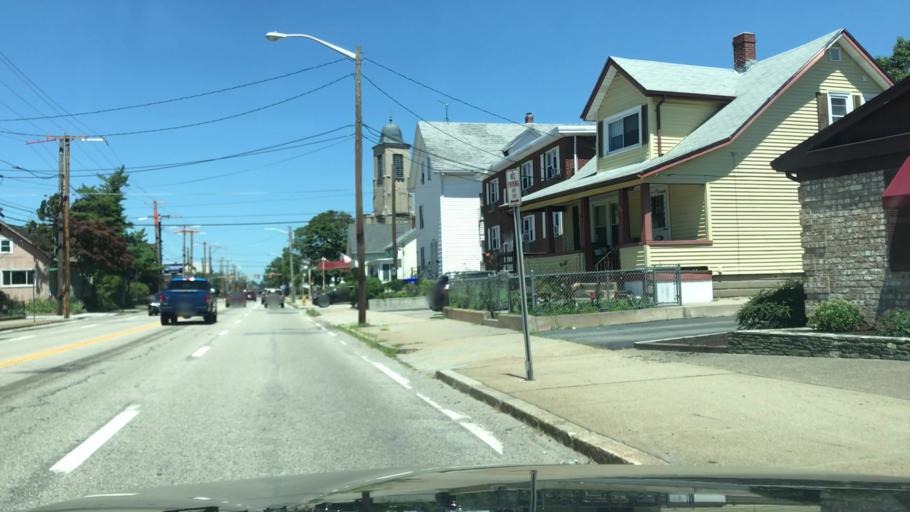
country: US
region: Massachusetts
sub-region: Bristol County
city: North Seekonk
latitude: 41.8859
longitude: -71.3541
